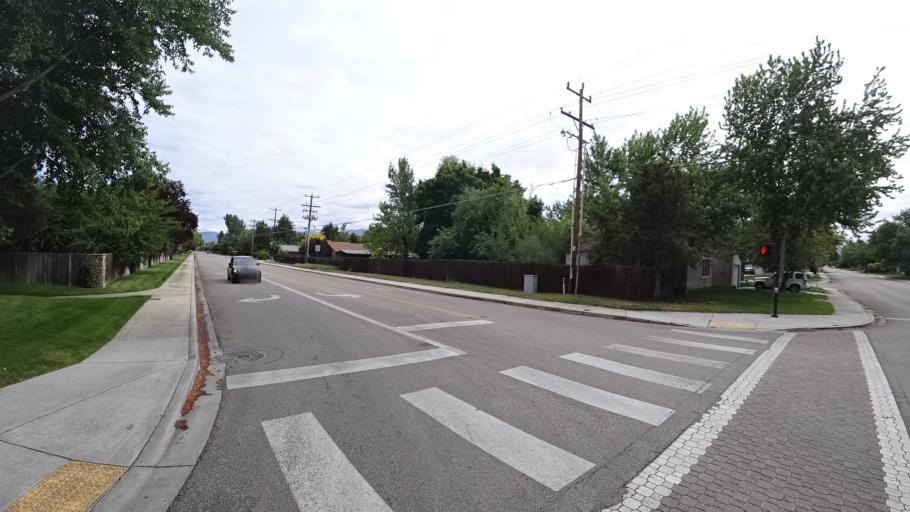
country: US
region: Idaho
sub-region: Ada County
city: Boise
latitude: 43.5679
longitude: -116.1735
